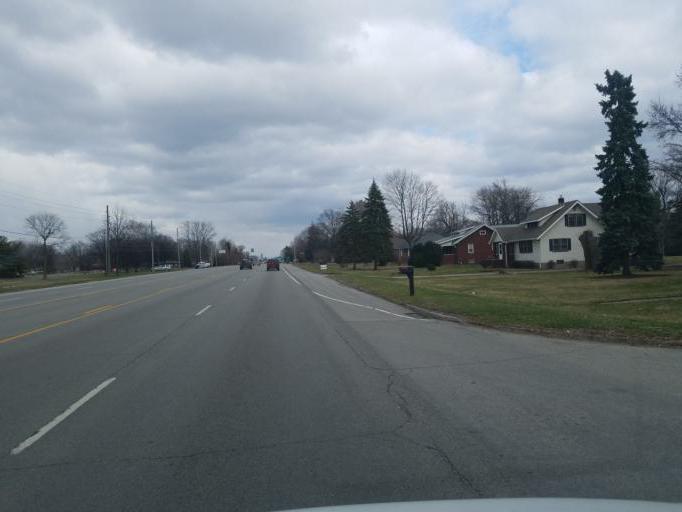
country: US
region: Indiana
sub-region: Marion County
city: Speedway
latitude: 39.7644
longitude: -86.2814
